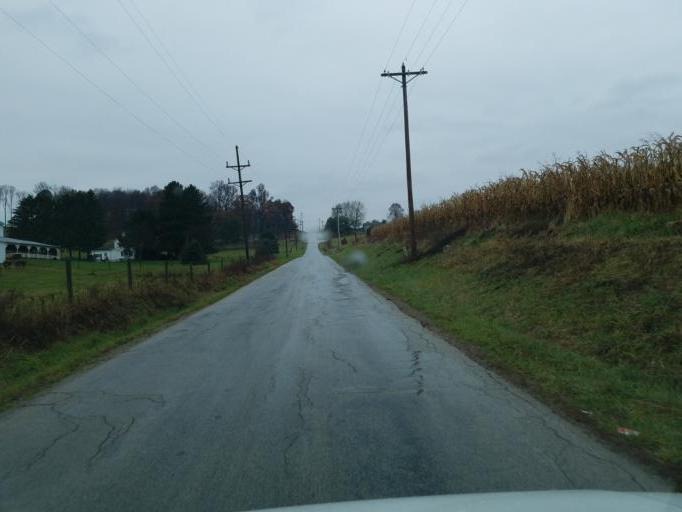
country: US
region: Ohio
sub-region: Sandusky County
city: Bellville
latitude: 40.5916
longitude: -82.5480
